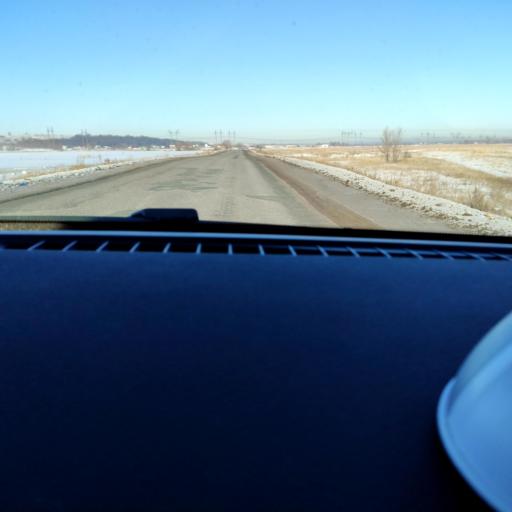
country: RU
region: Samara
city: Spiridonovka
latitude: 53.1375
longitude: 50.6028
